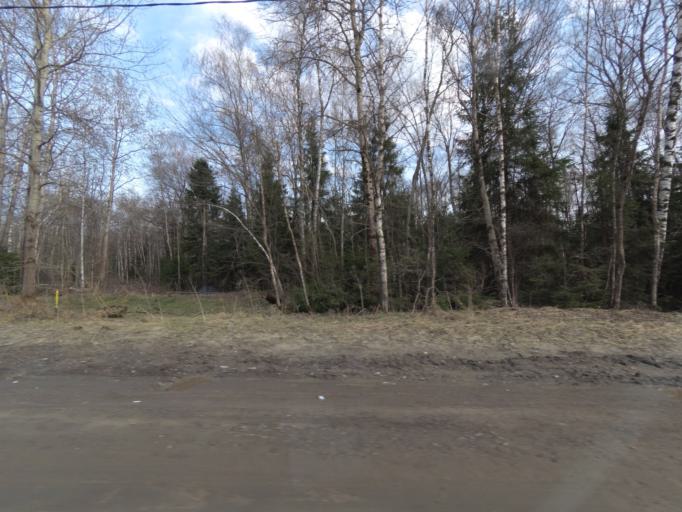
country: RU
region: Moskovskaya
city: Lobnya
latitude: 55.9984
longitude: 37.4230
